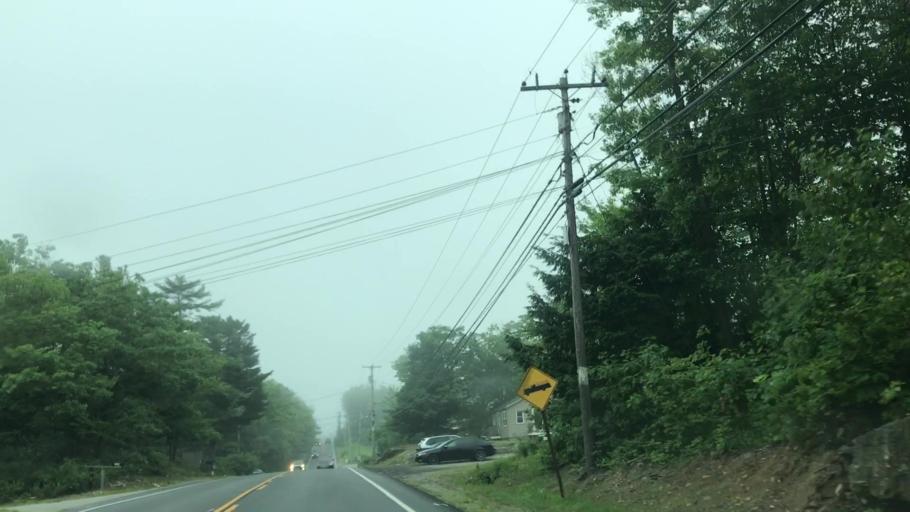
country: US
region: Maine
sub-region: Sagadahoc County
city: Bath
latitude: 43.9038
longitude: -69.8522
